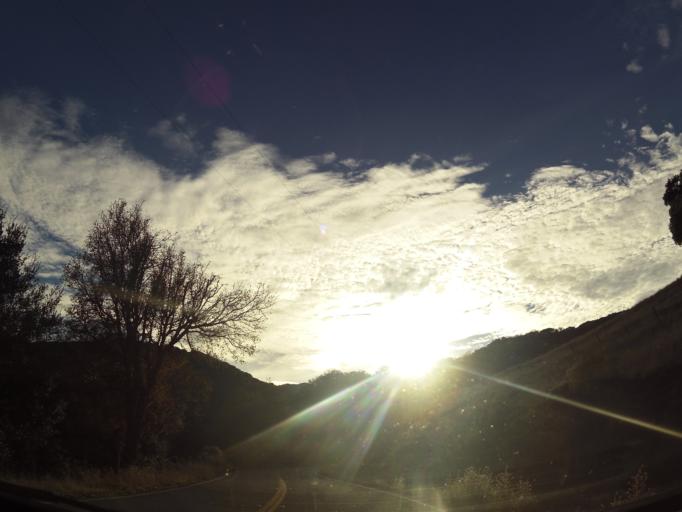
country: US
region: California
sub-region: Santa Clara County
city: Seven Trees
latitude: 37.1625
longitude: -121.8413
